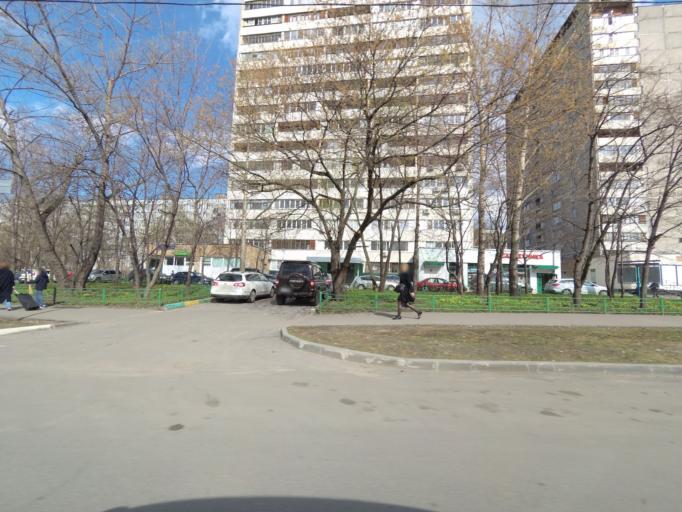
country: RU
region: Moscow
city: Gol'yanovo
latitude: 55.8208
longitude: 37.8263
